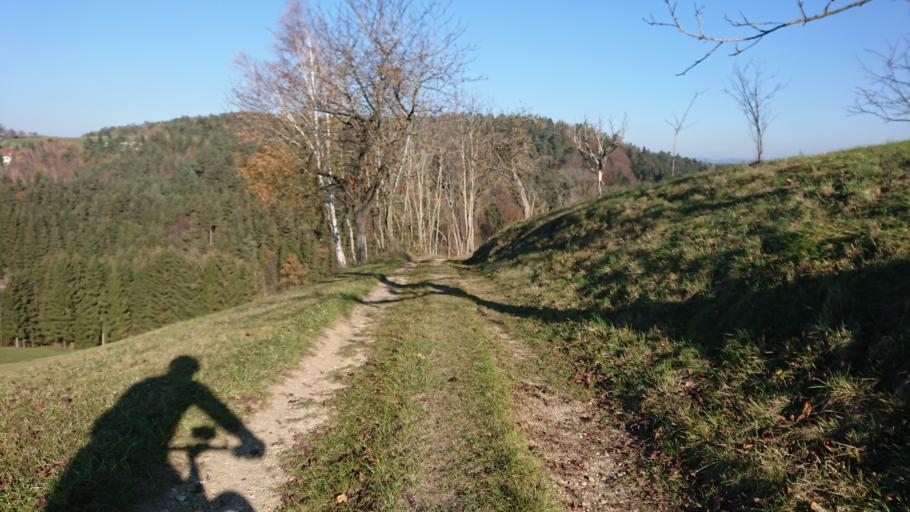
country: AT
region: Upper Austria
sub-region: Politischer Bezirk Urfahr-Umgebung
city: Feldkirchen an der Donau
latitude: 48.4057
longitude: 14.0521
